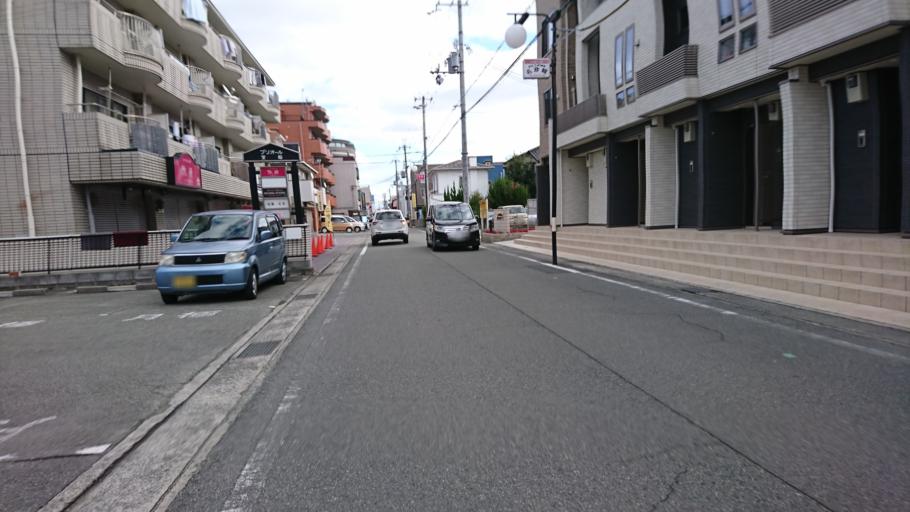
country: JP
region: Hyogo
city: Kakogawacho-honmachi
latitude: 34.7859
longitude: 134.8106
